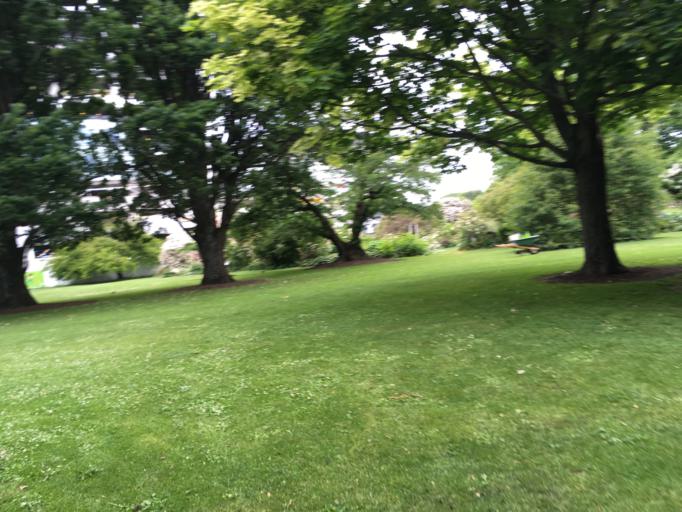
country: NZ
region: Canterbury
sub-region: Christchurch City
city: Christchurch
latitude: -43.5327
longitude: 172.6224
